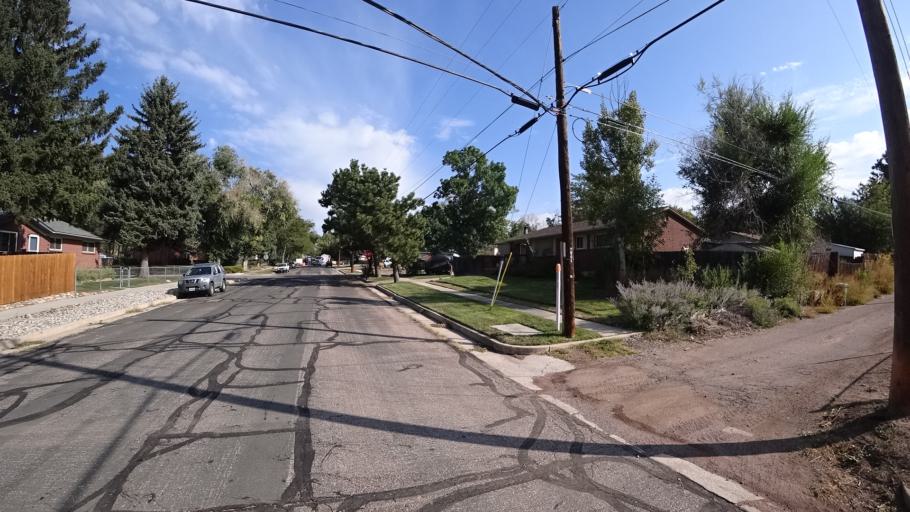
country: US
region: Colorado
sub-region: El Paso County
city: Colorado Springs
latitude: 38.8564
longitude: -104.7848
